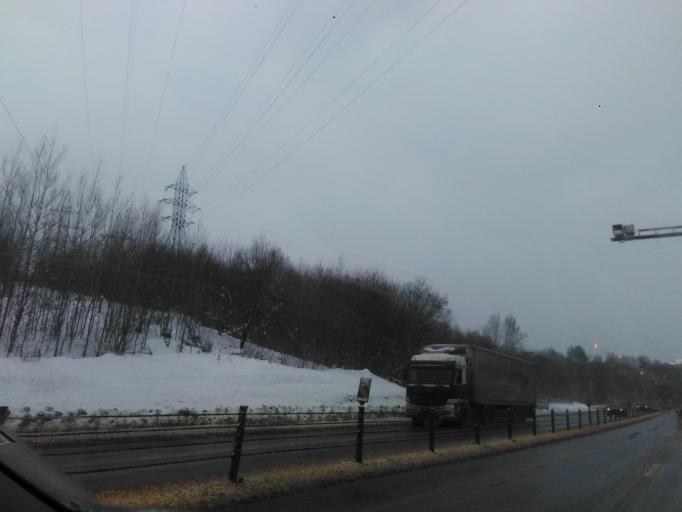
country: RU
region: Moskovskaya
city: Dedenevo
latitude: 56.2501
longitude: 37.5173
